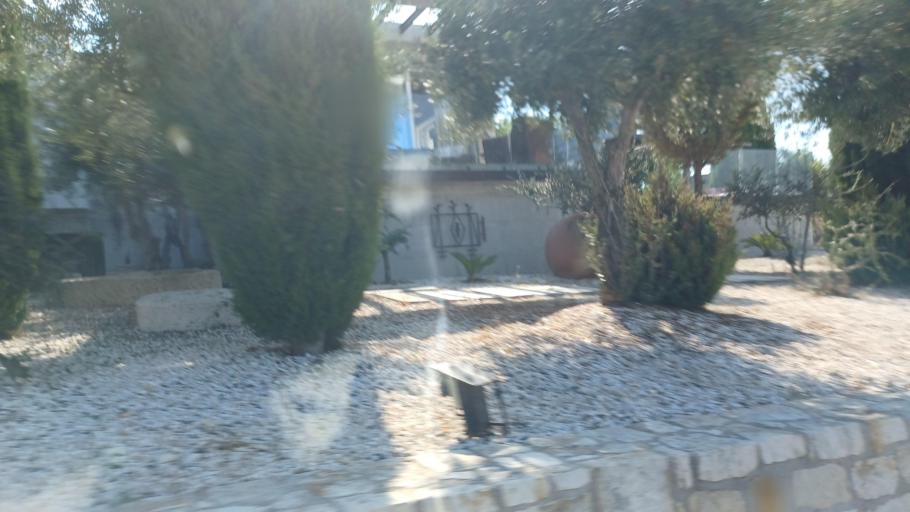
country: CY
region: Pafos
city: Pegeia
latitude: 34.9032
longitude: 32.4224
